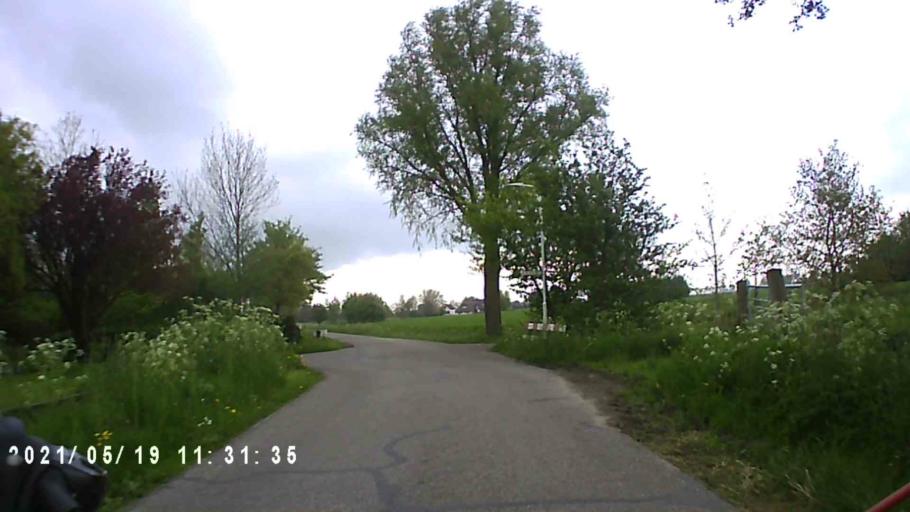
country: NL
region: Friesland
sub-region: Gemeente Kollumerland en Nieuwkruisland
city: Kollum
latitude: 53.2745
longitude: 6.1739
